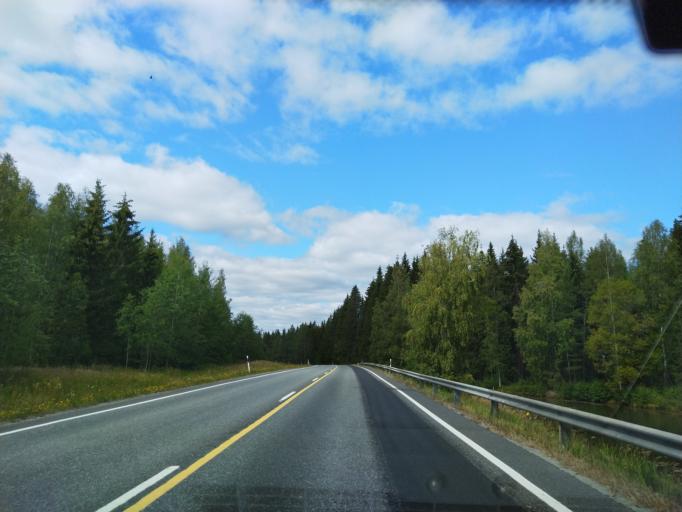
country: FI
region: Haeme
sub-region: Haemeenlinna
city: Tervakoski
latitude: 60.7436
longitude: 24.6688
